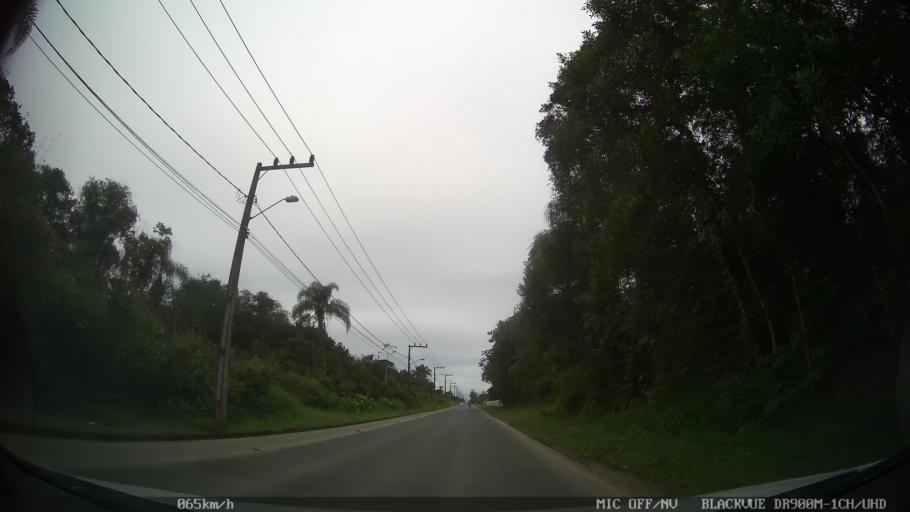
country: BR
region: Santa Catarina
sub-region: Joinville
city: Joinville
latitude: -26.3139
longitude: -48.9186
